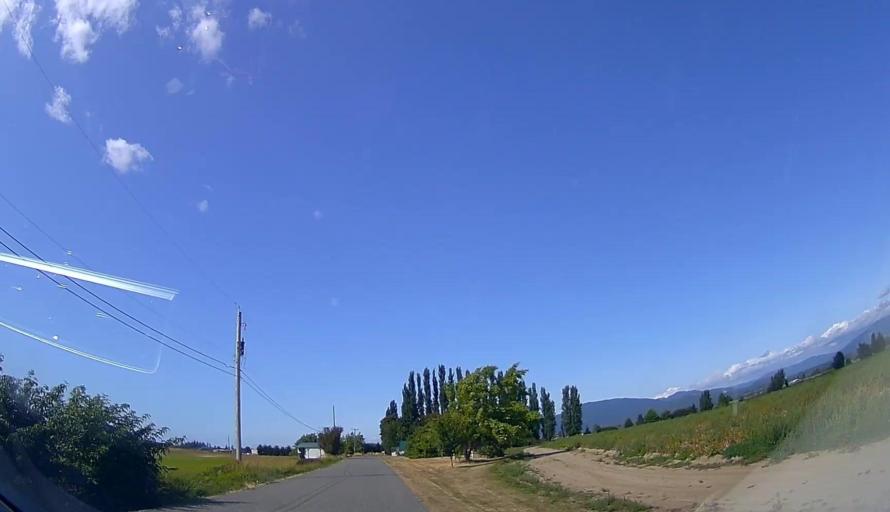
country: US
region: Washington
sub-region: Skagit County
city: Burlington
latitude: 48.5175
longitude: -122.4327
